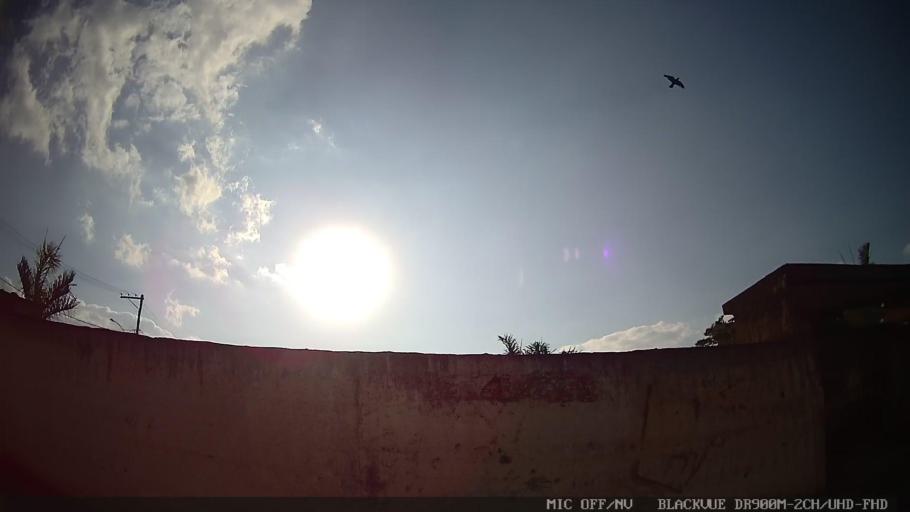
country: BR
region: Sao Paulo
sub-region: Cabreuva
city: Cabreuva
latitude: -23.2676
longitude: -47.0609
